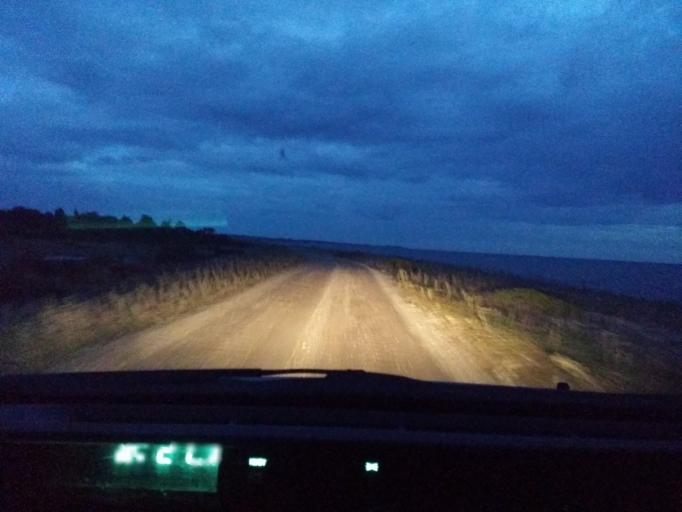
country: SE
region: Kalmar
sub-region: Borgholms Kommun
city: Borgholm
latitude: 57.1338
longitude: 16.9022
